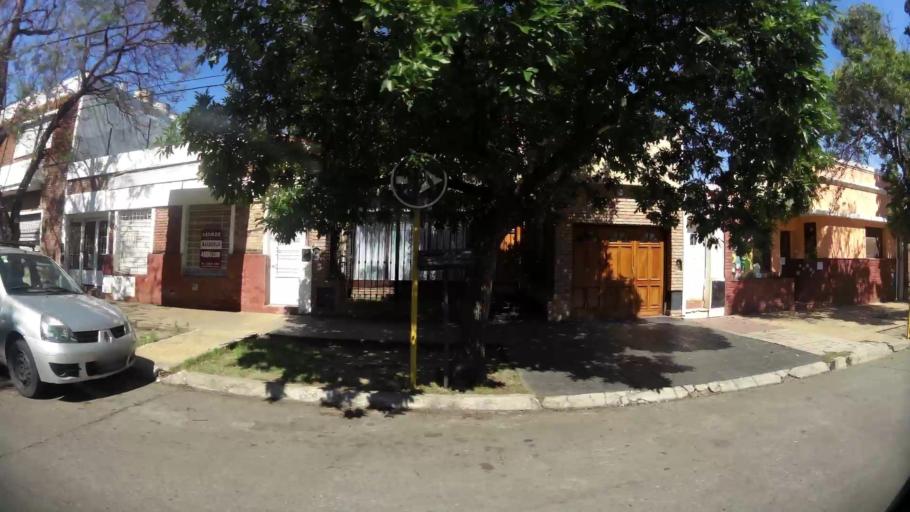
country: AR
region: Cordoba
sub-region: Departamento de Capital
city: Cordoba
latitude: -31.4195
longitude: -64.1695
